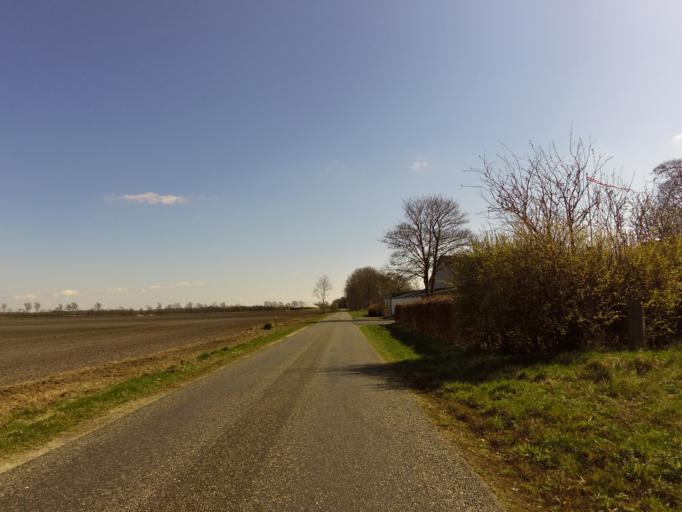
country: DK
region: South Denmark
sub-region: Esbjerg Kommune
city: Ribe
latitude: 55.3417
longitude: 8.8596
